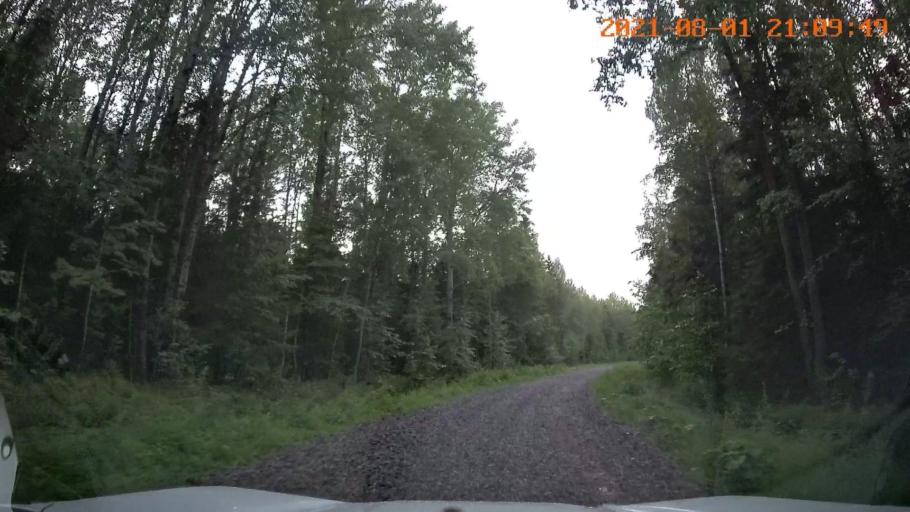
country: RU
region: Leningrad
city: Syas'stroy
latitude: 60.5118
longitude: 32.6445
